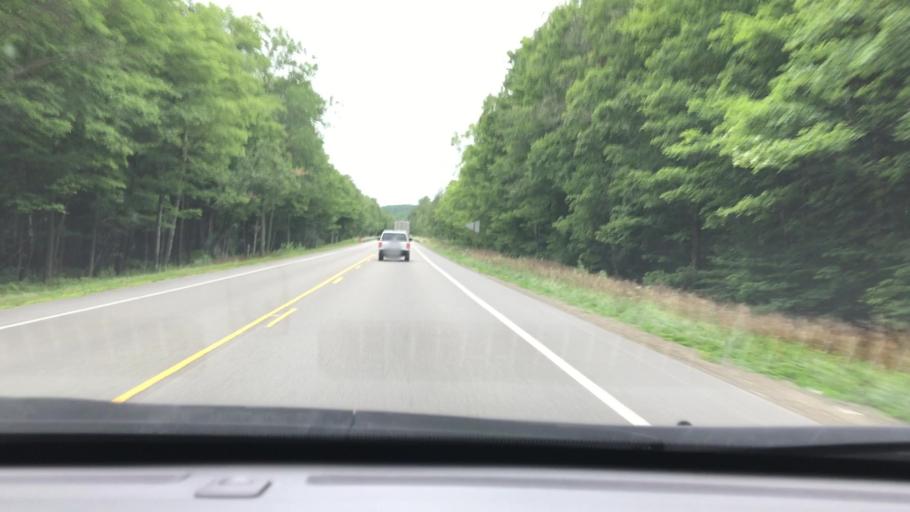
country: US
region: Pennsylvania
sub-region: McKean County
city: Kane
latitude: 41.6792
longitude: -78.6863
